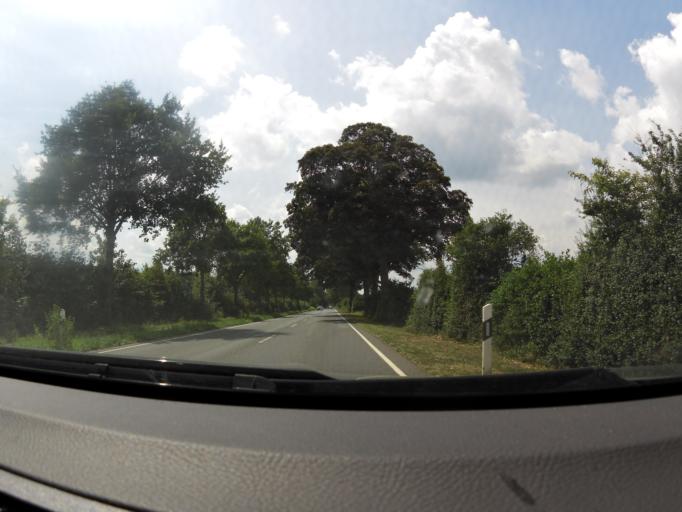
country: DE
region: North Rhine-Westphalia
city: Geldern
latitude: 51.5576
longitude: 6.3352
